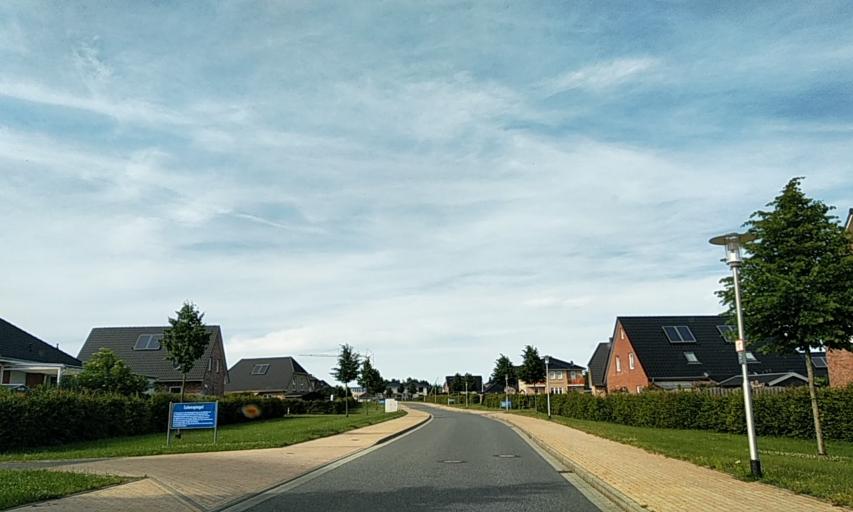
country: DE
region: Schleswig-Holstein
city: Schleswig
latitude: 54.5342
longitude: 9.5674
